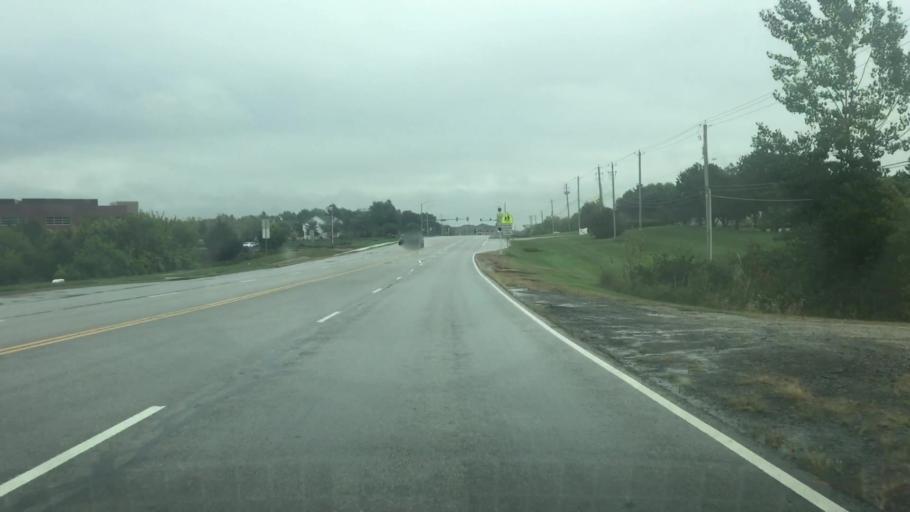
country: US
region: Kansas
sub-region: Johnson County
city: Lenexa
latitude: 38.9710
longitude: -94.7973
